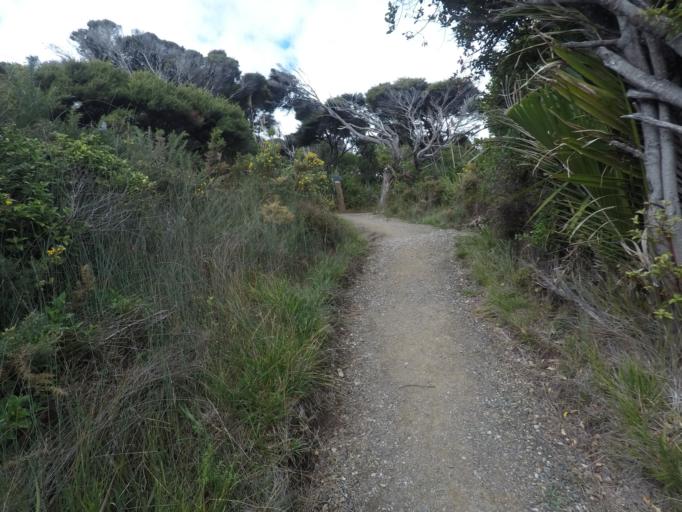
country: NZ
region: Auckland
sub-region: Auckland
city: Titirangi
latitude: -37.0415
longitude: 174.5112
